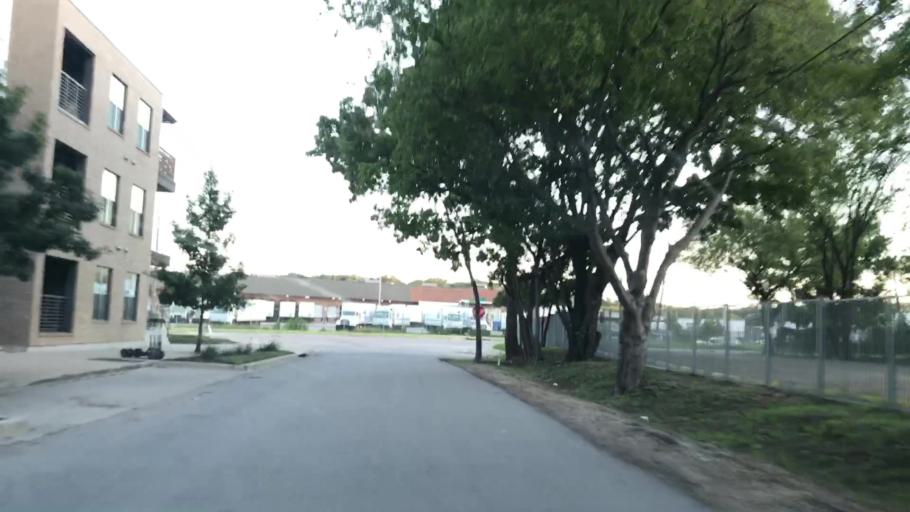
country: US
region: Texas
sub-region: Dallas County
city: Dallas
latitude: 32.7719
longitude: -96.8313
